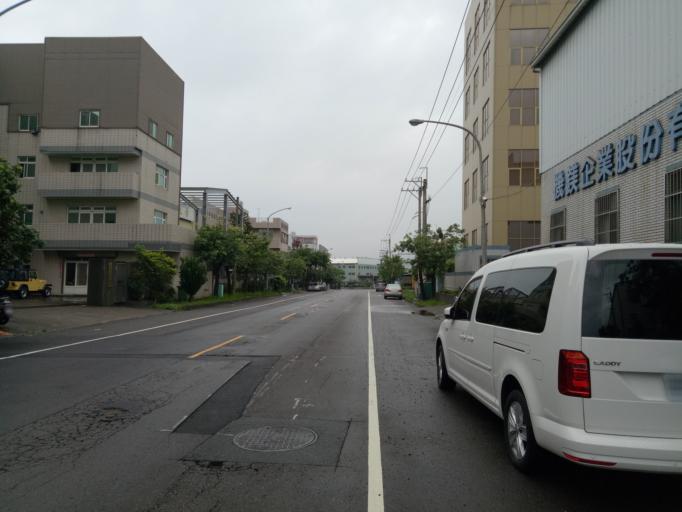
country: TW
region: Taiwan
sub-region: Taichung City
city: Taichung
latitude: 24.1048
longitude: 120.7178
